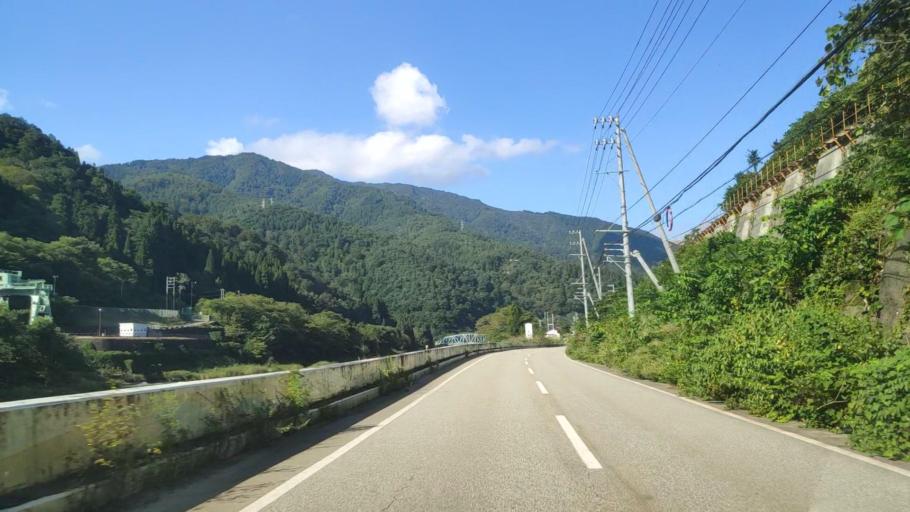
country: JP
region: Gifu
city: Takayama
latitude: 36.3225
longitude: 137.1354
